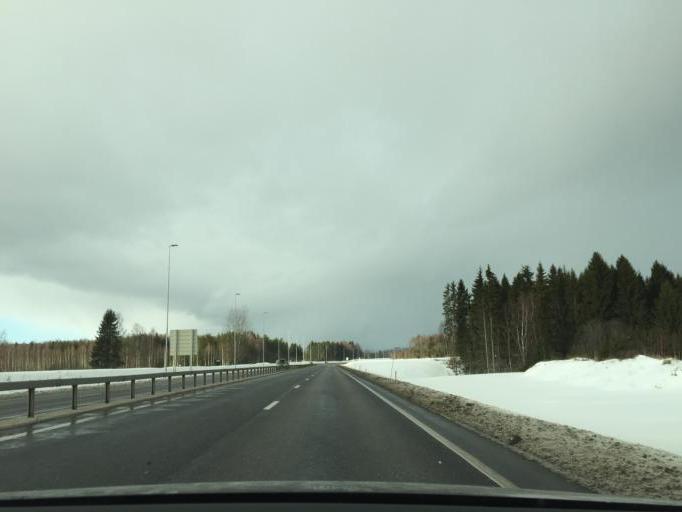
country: NO
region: Hedmark
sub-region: Kongsvinger
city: Spetalen
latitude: 60.2130
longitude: 11.8798
